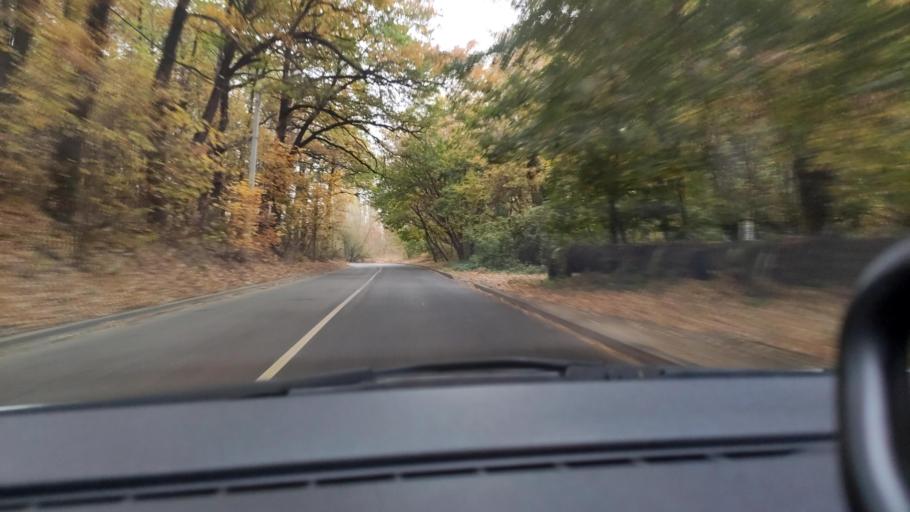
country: RU
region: Voronezj
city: Voronezh
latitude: 51.7218
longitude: 39.2364
